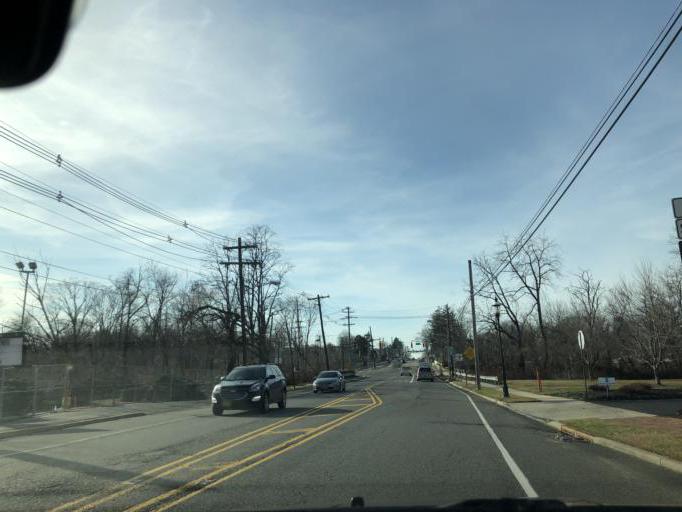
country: US
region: New Jersey
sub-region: Burlington County
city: Maple Shade
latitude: 39.9571
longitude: -74.9856
